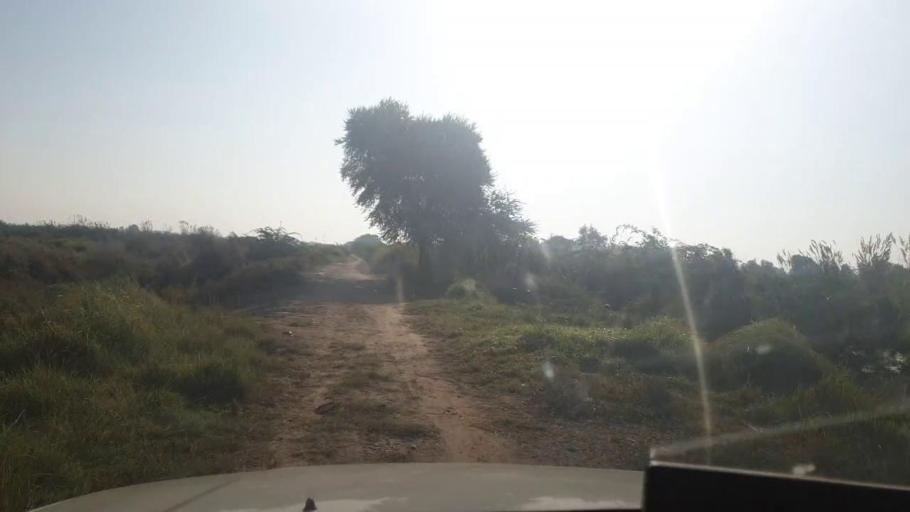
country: PK
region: Sindh
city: Mirpur Sakro
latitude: 24.5787
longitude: 67.7274
